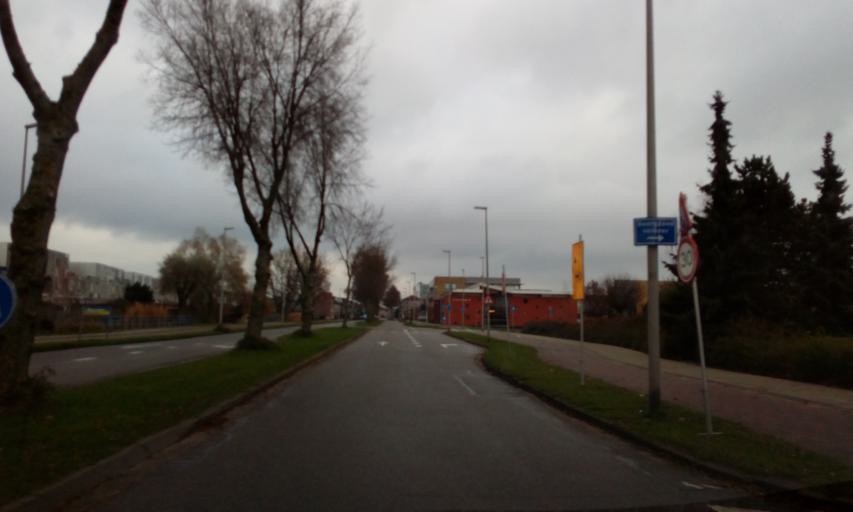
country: NL
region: South Holland
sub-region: Gemeente Zoetermeer
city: Zoetermeer
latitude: 52.0368
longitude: 4.4967
